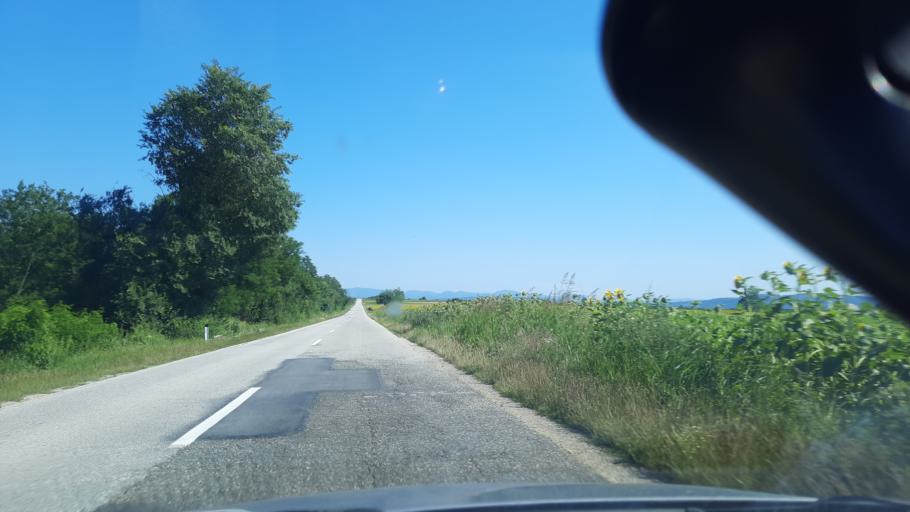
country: RS
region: Central Serbia
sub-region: Branicevski Okrug
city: Malo Crnice
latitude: 44.5725
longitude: 21.4253
